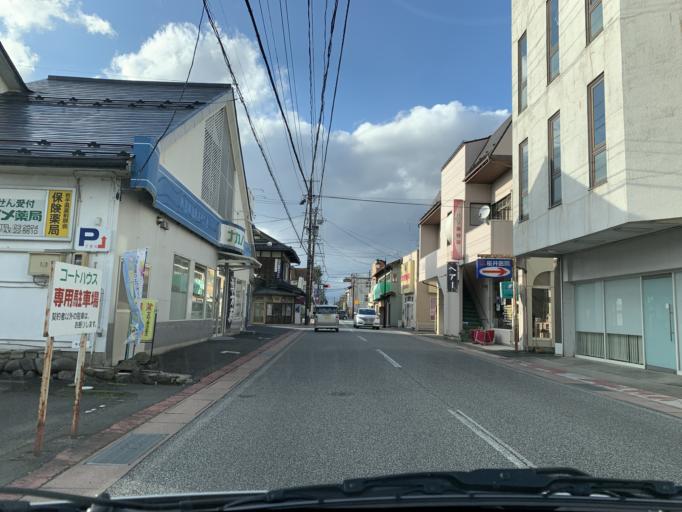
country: JP
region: Iwate
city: Mizusawa
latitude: 39.1428
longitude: 141.1405
